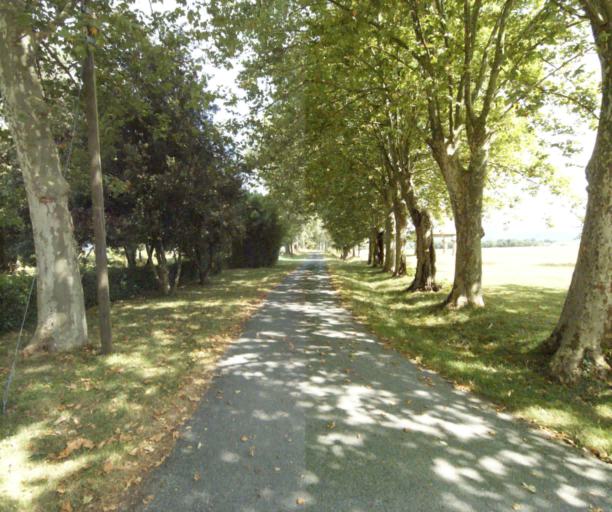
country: FR
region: Midi-Pyrenees
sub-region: Departement du Tarn
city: Soreze
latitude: 43.5078
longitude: 2.0500
